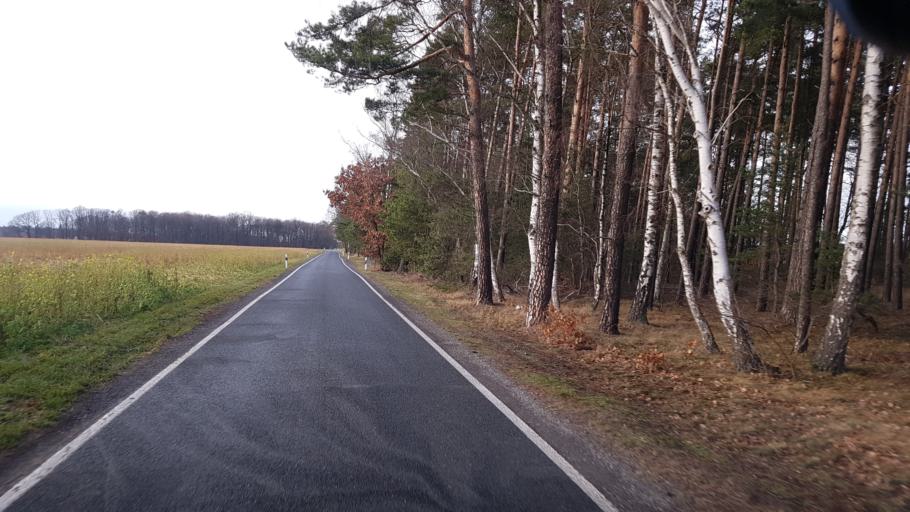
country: DE
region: Brandenburg
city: Bronkow
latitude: 51.6683
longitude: 13.9285
